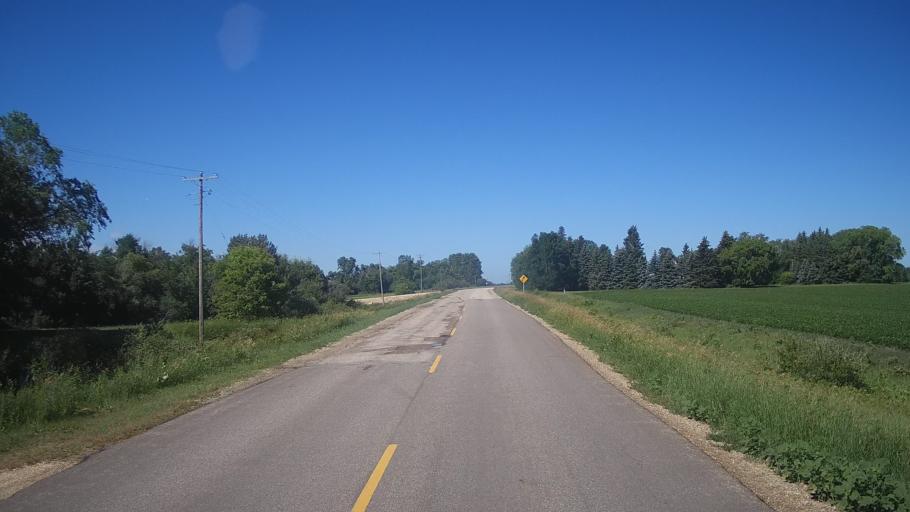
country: CA
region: Manitoba
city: Portage la Prairie
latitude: 50.0454
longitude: -98.0247
